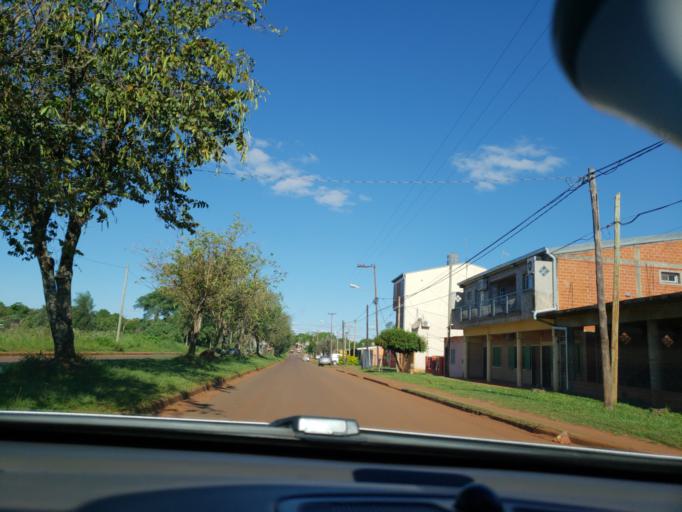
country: AR
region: Misiones
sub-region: Departamento de Capital
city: Posadas
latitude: -27.3828
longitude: -55.9443
